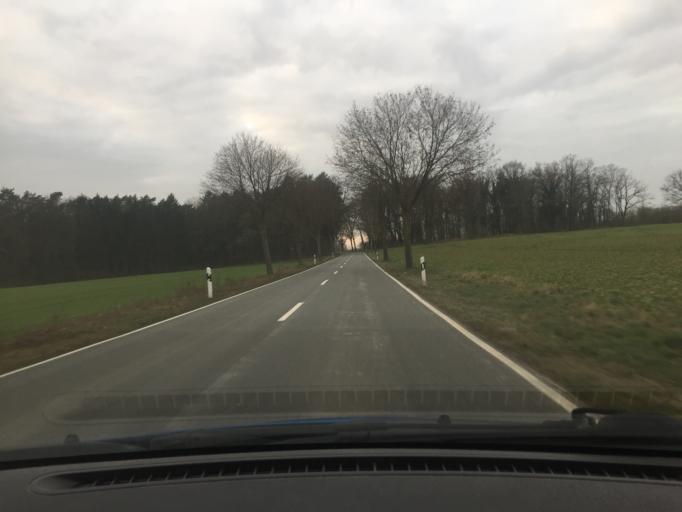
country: DE
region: Lower Saxony
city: Oetzen
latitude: 53.0391
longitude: 10.6615
